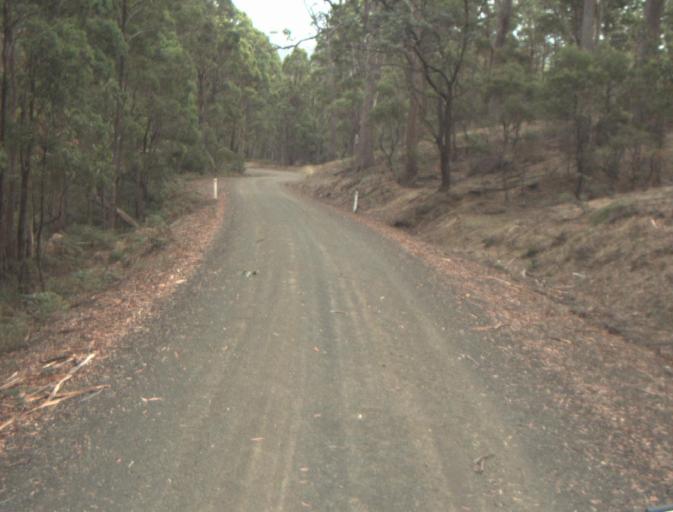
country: AU
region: Tasmania
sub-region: Northern Midlands
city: Evandale
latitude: -41.4904
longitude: 147.5463
